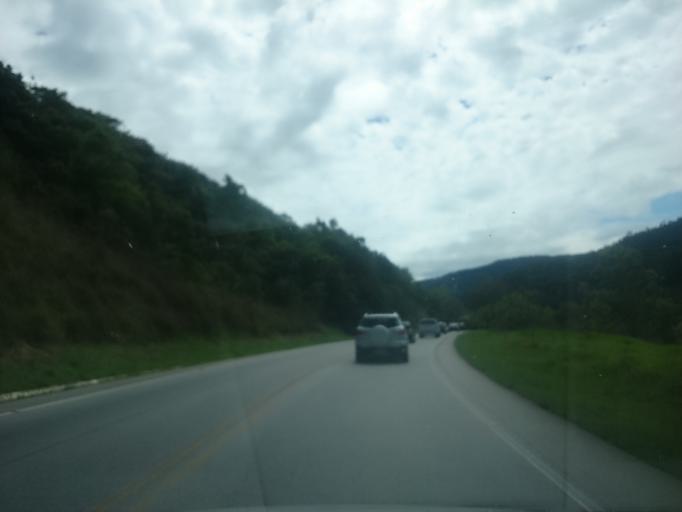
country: BR
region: Santa Catarina
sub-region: Anitapolis
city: Anitapolis
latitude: -27.7005
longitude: -49.2913
